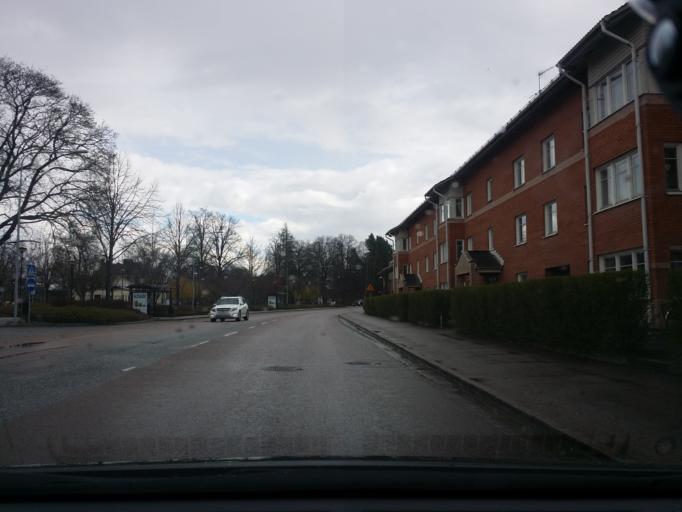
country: SE
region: Uppsala
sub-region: Enkopings Kommun
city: Enkoping
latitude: 59.6445
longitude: 17.0852
